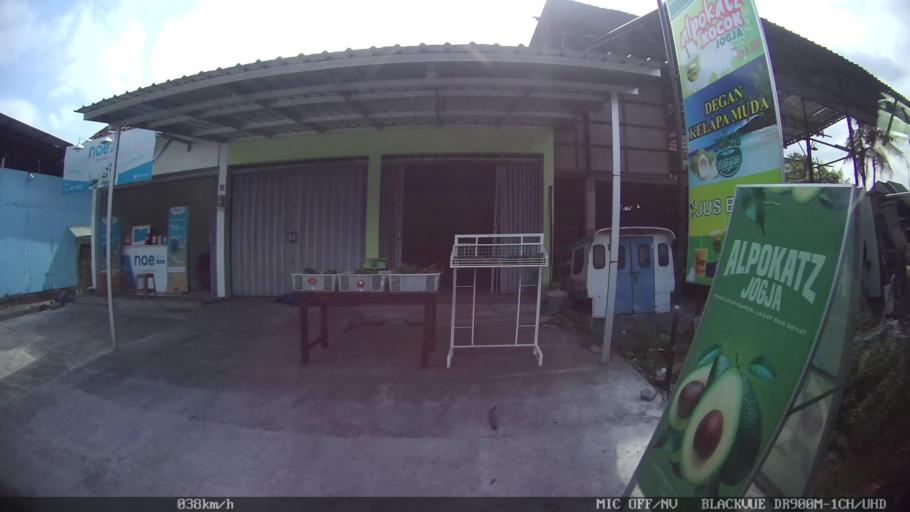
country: ID
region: Daerah Istimewa Yogyakarta
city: Depok
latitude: -7.7389
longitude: 110.4206
